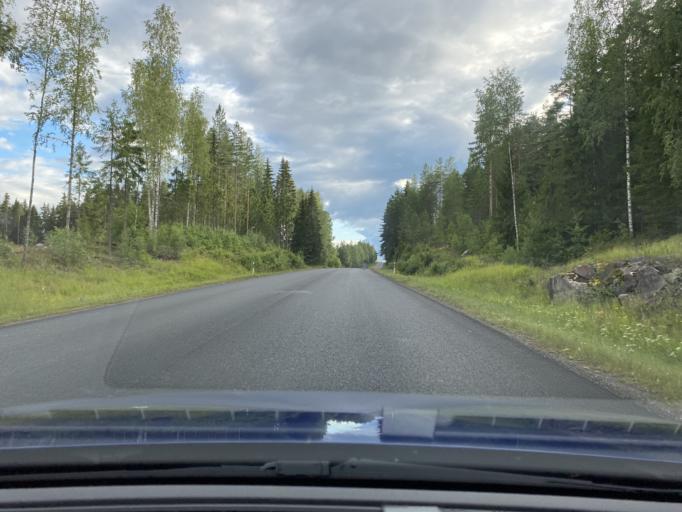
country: FI
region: Haeme
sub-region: Haemeenlinna
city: Haemeenlinna
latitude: 60.9408
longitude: 24.3846
